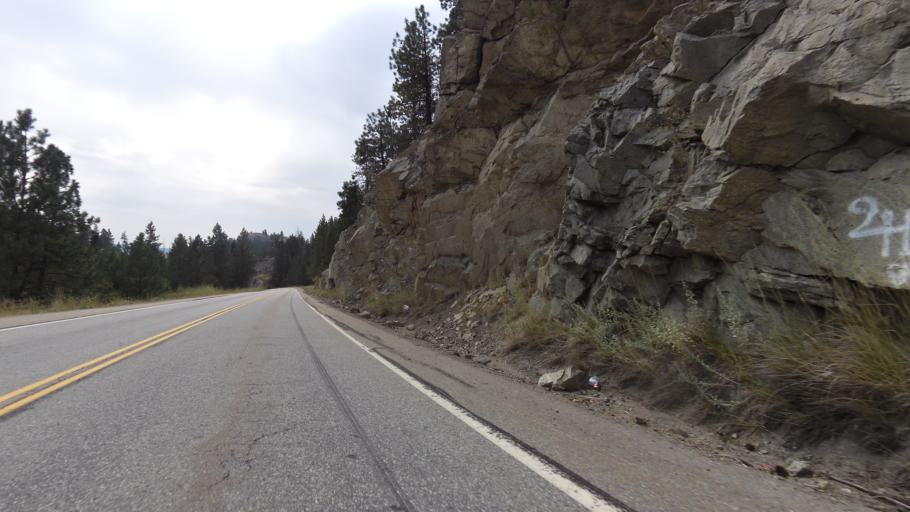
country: CA
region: British Columbia
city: Osoyoos
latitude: 49.0212
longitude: -119.3920
